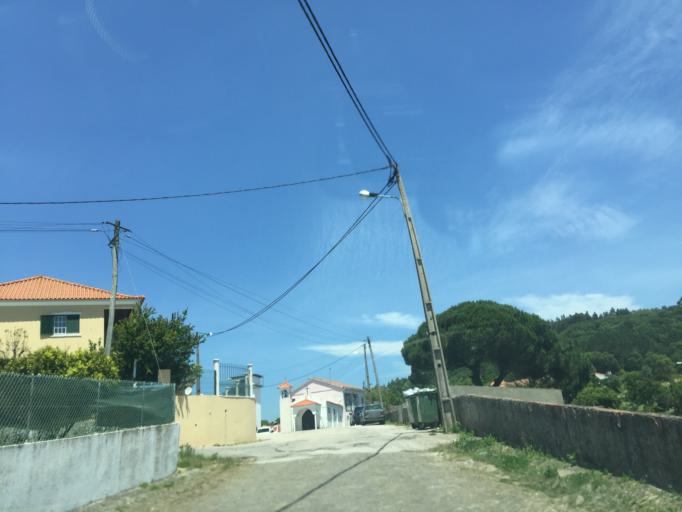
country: PT
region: Lisbon
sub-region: Mafra
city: Venda do Pinheiro
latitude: 38.8953
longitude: -9.2328
